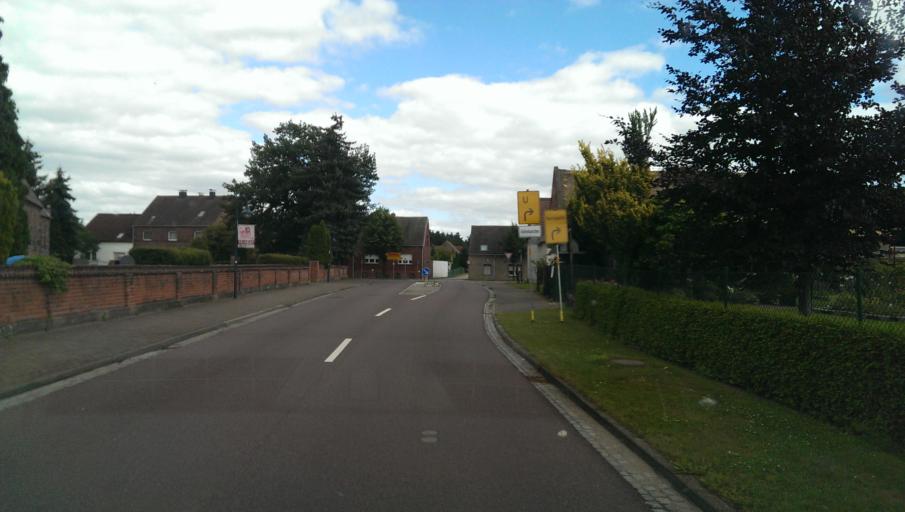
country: DE
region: Saxony-Anhalt
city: Radis
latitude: 51.7845
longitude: 12.4856
